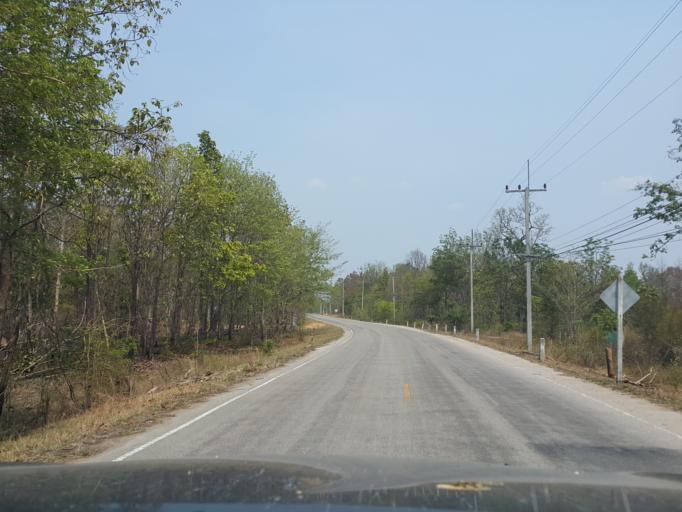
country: TH
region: Lampang
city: Mae Phrik
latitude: 17.5445
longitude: 99.1337
